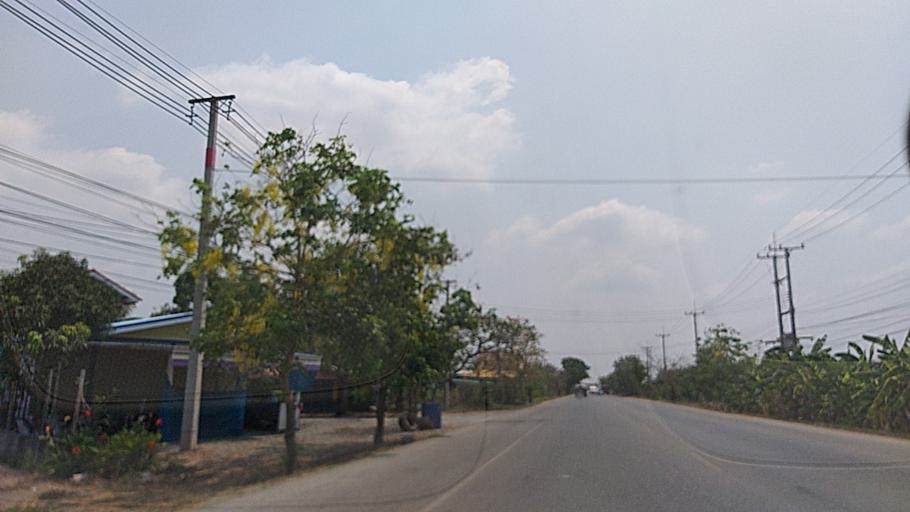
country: TH
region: Chachoengsao
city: Chachoengsao
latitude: 13.7545
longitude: 101.0758
